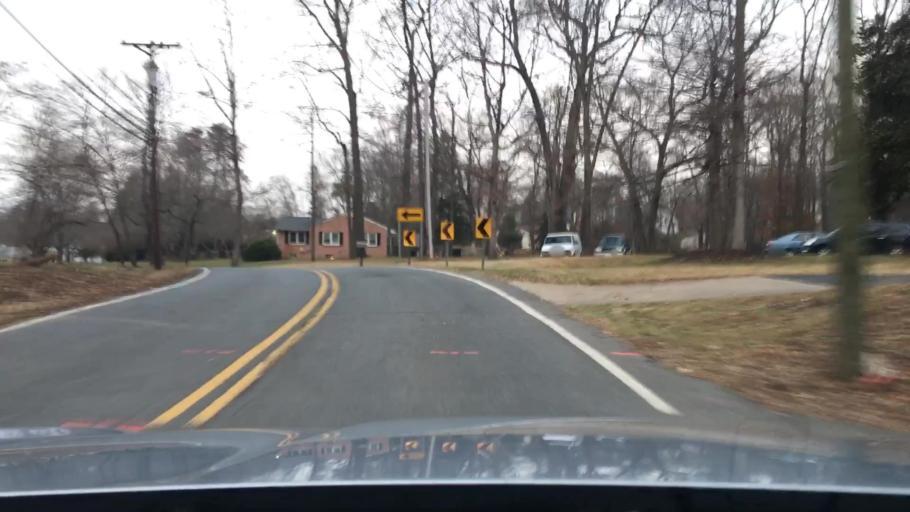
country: US
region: Maryland
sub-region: Prince George's County
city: Glenn Dale
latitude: 38.9961
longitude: -76.7756
